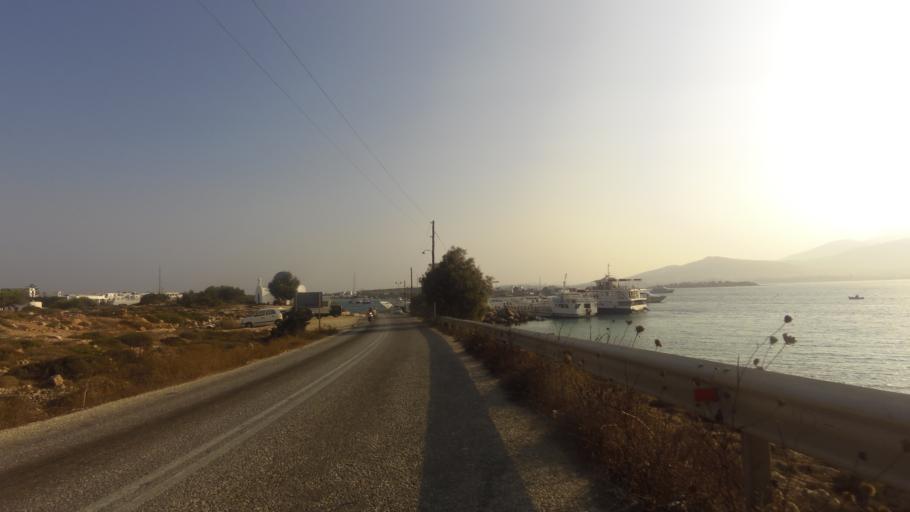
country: GR
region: South Aegean
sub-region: Nomos Kykladon
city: Antiparos
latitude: 37.0381
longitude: 25.0848
